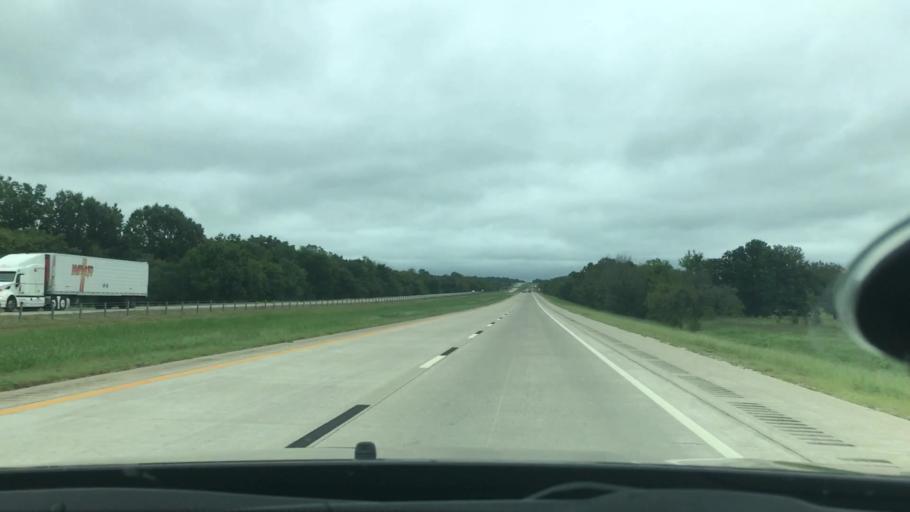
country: US
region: Oklahoma
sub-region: Muskogee County
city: Warner
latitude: 35.4823
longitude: -95.2589
